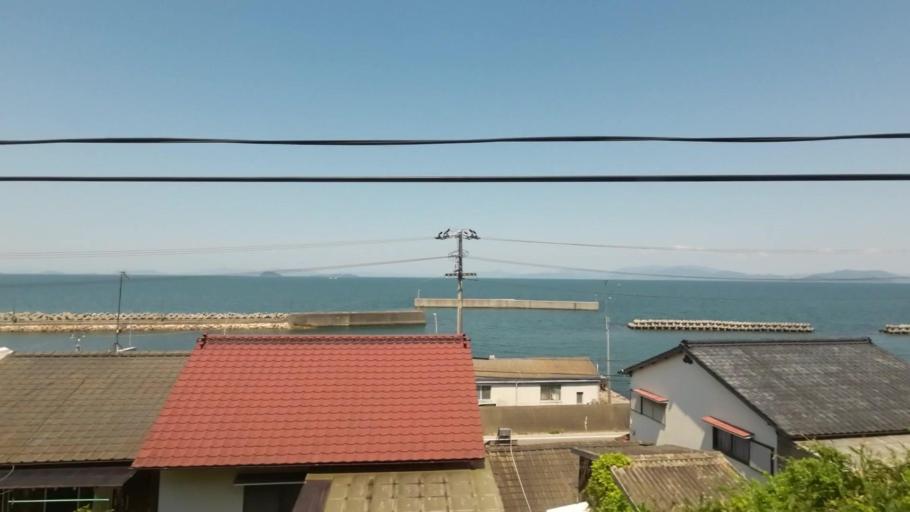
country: JP
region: Ehime
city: Hojo
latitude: 34.0219
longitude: 132.8170
